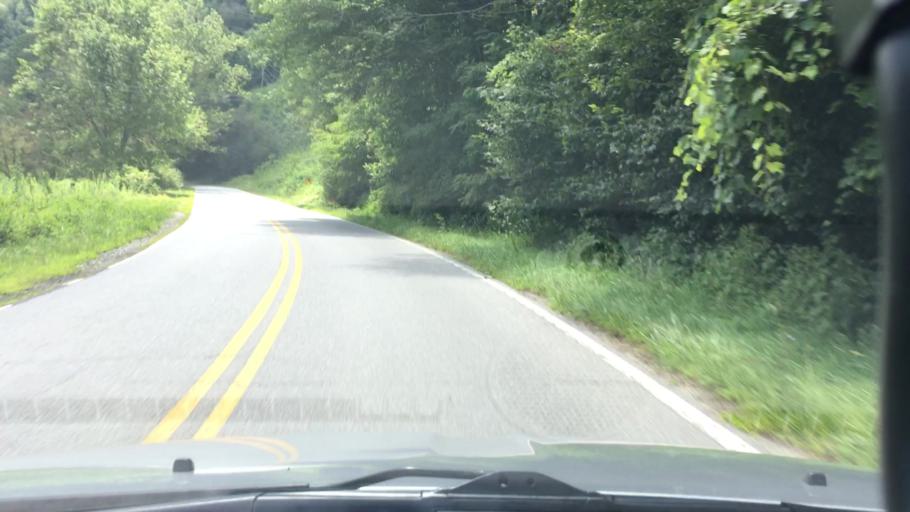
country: US
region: North Carolina
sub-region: Madison County
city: Mars Hill
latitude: 35.9166
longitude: -82.5467
